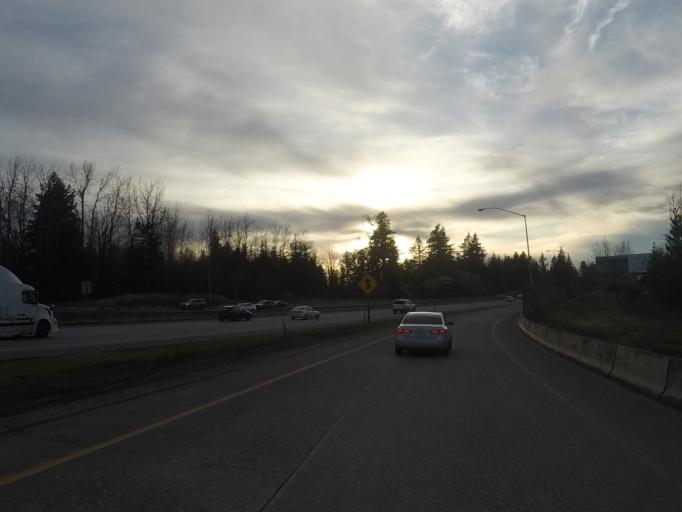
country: US
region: Oregon
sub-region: Multnomah County
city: Wood Village
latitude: 45.5401
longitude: -122.4211
